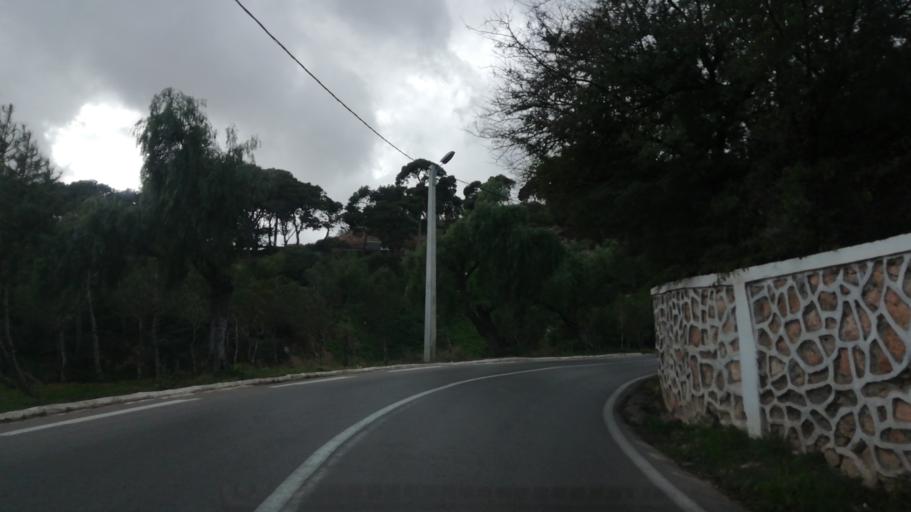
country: DZ
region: Oran
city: Oran
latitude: 35.7047
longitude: -0.6597
